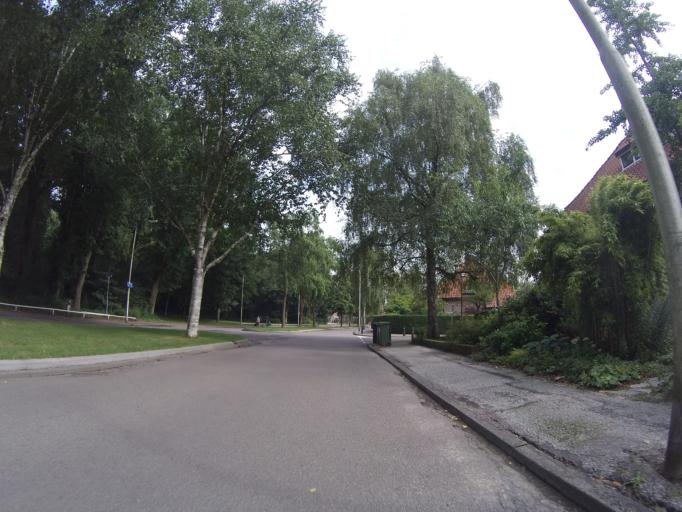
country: NL
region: Utrecht
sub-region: Gemeente Amersfoort
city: Amersfoort
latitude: 52.1392
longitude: 5.3748
